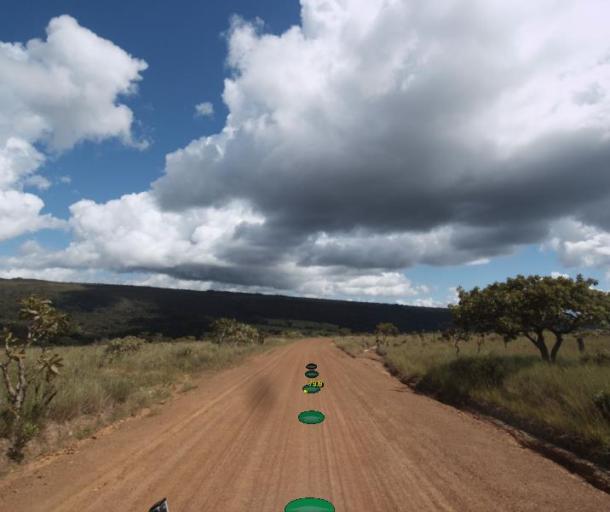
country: BR
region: Goias
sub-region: Pirenopolis
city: Pirenopolis
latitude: -15.7840
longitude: -48.8626
